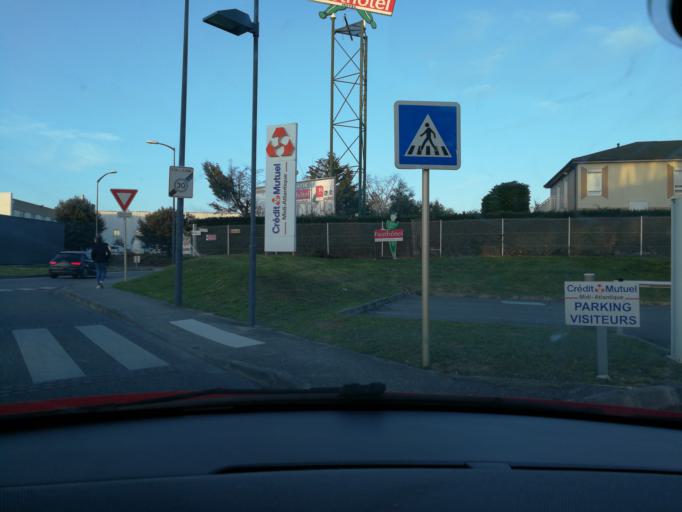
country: FR
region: Midi-Pyrenees
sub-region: Departement de la Haute-Garonne
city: Balma
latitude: 43.6293
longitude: 1.4864
